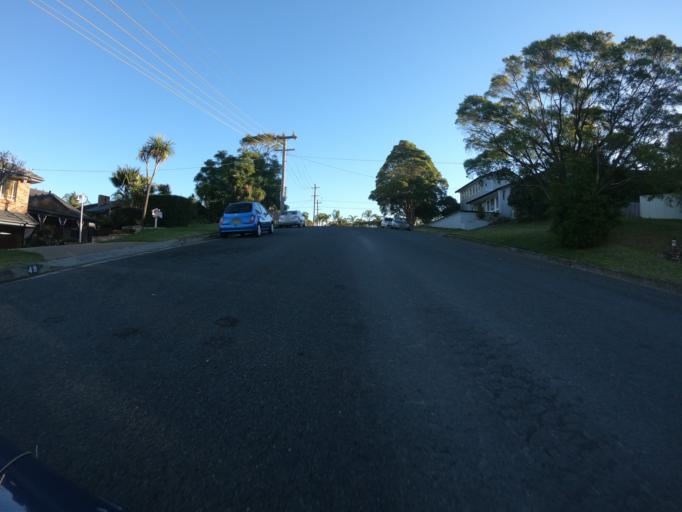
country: AU
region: New South Wales
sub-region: Wollongong
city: Cordeaux Heights
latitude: -34.4297
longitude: 150.8436
